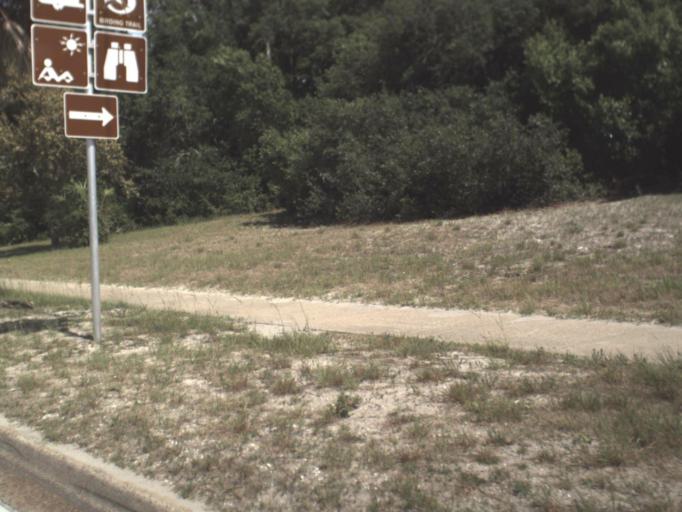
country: US
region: Florida
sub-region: Nassau County
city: Fernandina Beach
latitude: 30.6679
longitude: -81.4337
